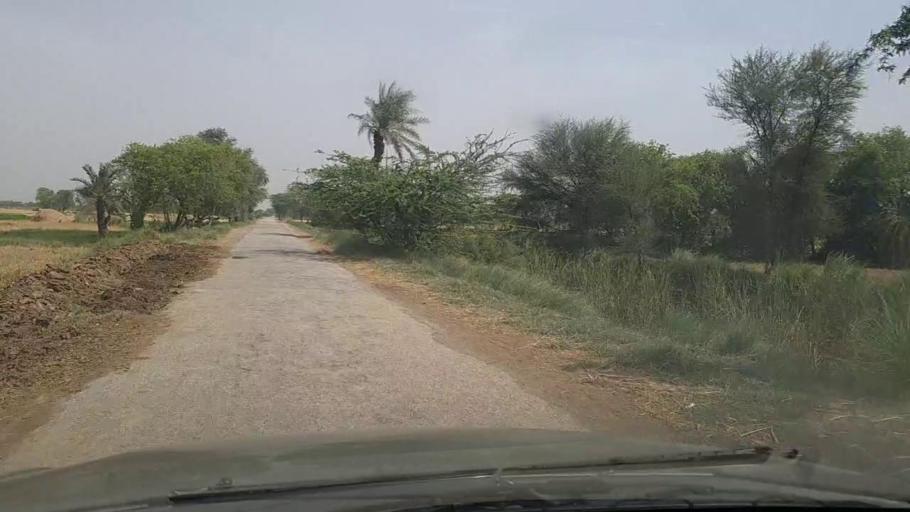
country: PK
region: Sindh
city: Lakhi
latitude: 27.8403
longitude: 68.7632
